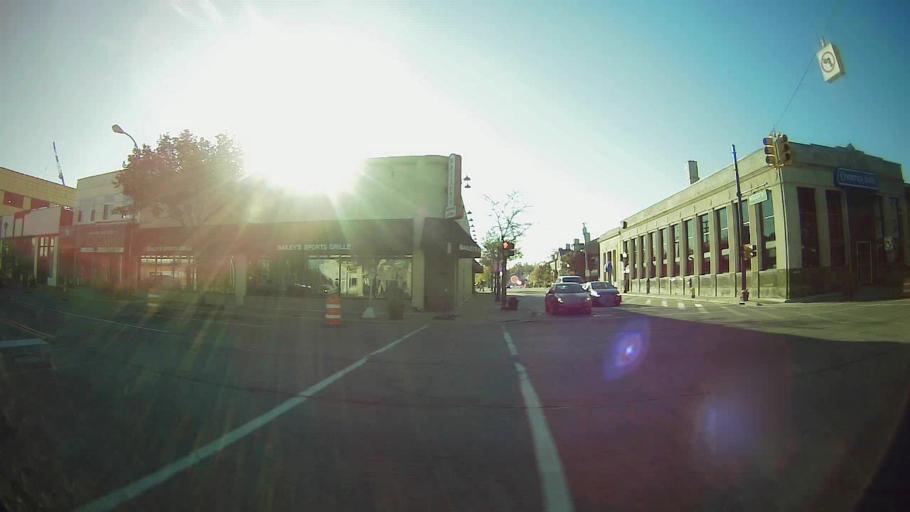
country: US
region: Michigan
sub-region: Wayne County
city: Dearborn Heights
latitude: 42.3054
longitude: -83.2477
